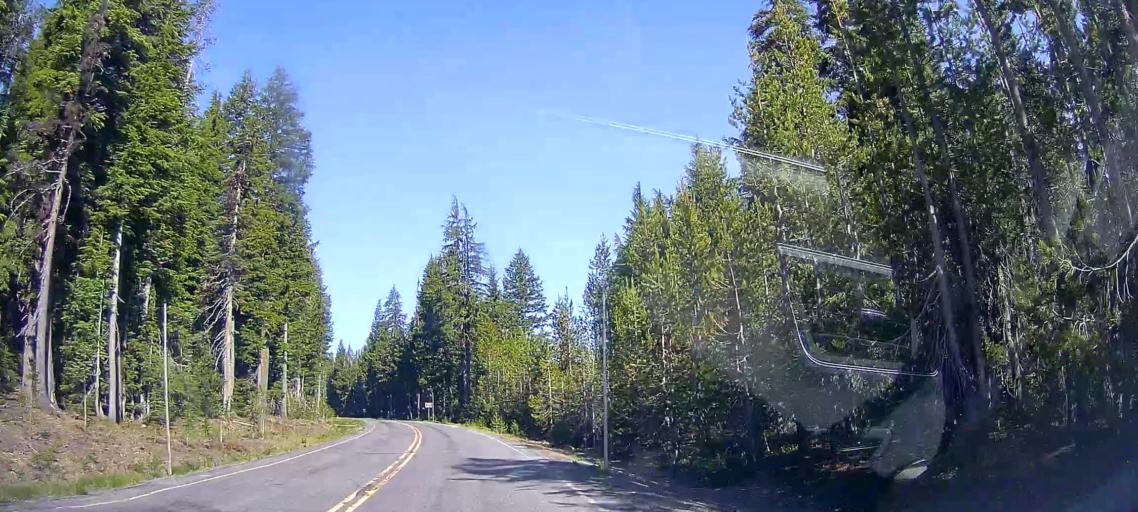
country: US
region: Oregon
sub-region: Jackson County
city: Shady Cove
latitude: 42.8596
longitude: -122.1561
